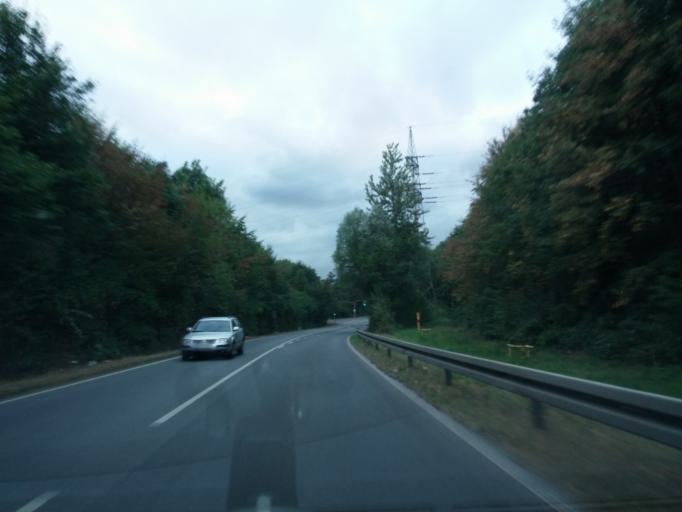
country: DE
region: North Rhine-Westphalia
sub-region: Regierungsbezirk Munster
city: Gladbeck
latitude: 51.5647
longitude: 7.0299
